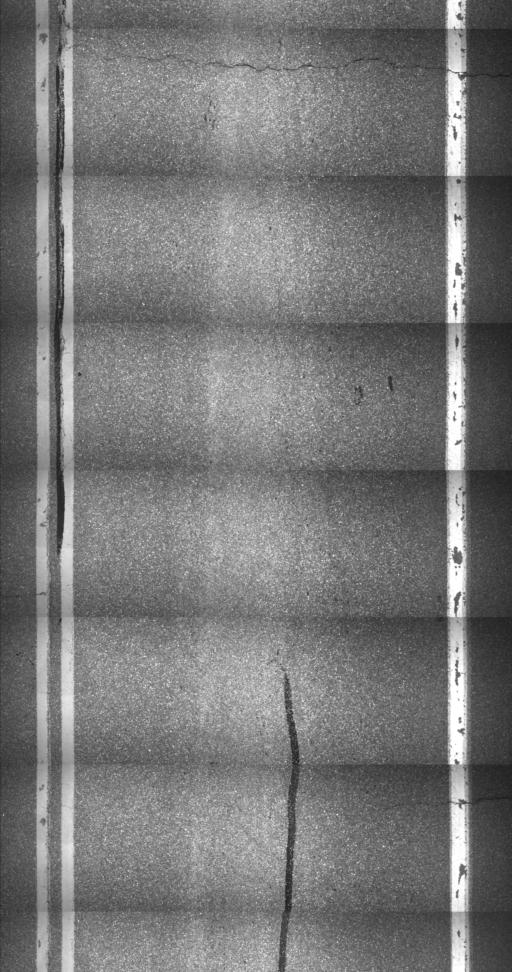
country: US
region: Vermont
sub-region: Chittenden County
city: Jericho
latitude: 44.5868
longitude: -73.0154
